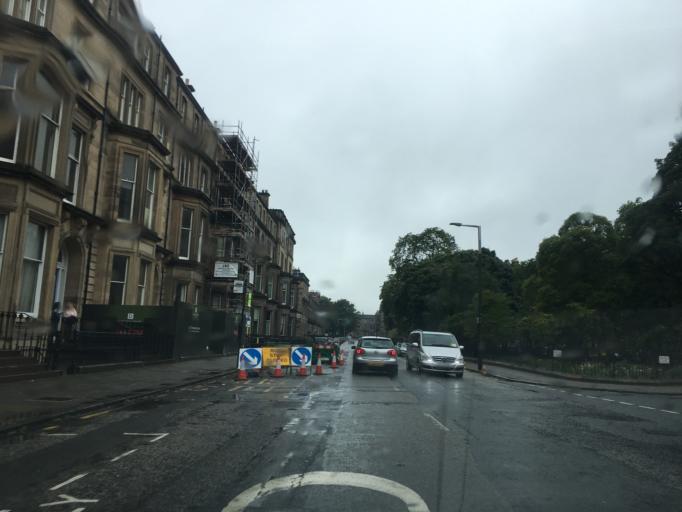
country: GB
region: Scotland
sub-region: Edinburgh
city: Edinburgh
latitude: 55.9512
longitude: -3.2134
